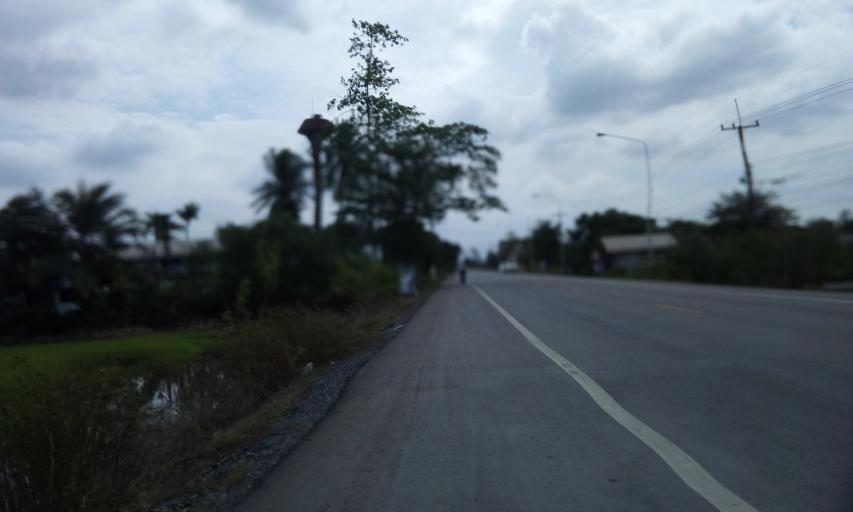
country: TH
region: Pathum Thani
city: Ban Lam Luk Ka
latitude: 14.0346
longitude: 100.8440
